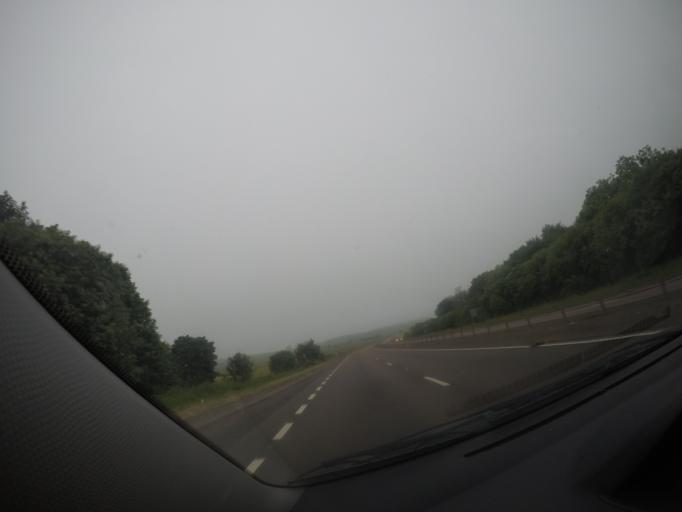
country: GB
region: Scotland
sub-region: Dundee City
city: Dundee
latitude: 56.5353
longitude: -2.9466
